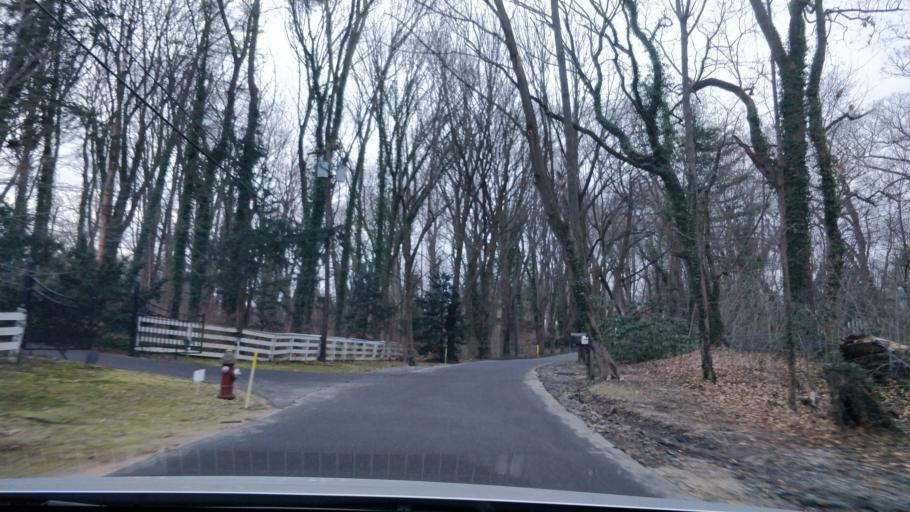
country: US
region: New York
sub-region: Nassau County
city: Oyster Bay Cove
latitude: 40.8695
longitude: -73.5177
